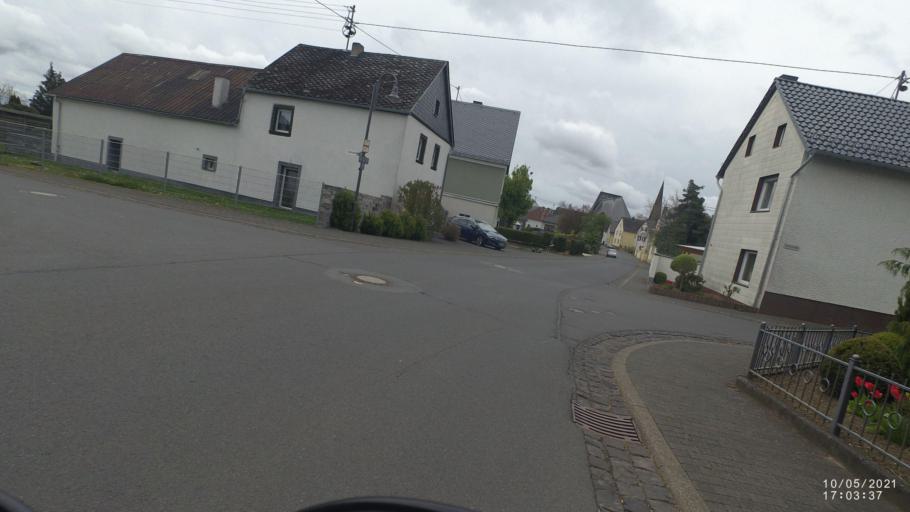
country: DE
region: Rheinland-Pfalz
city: Nachtsheim
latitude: 50.3197
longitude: 7.0618
